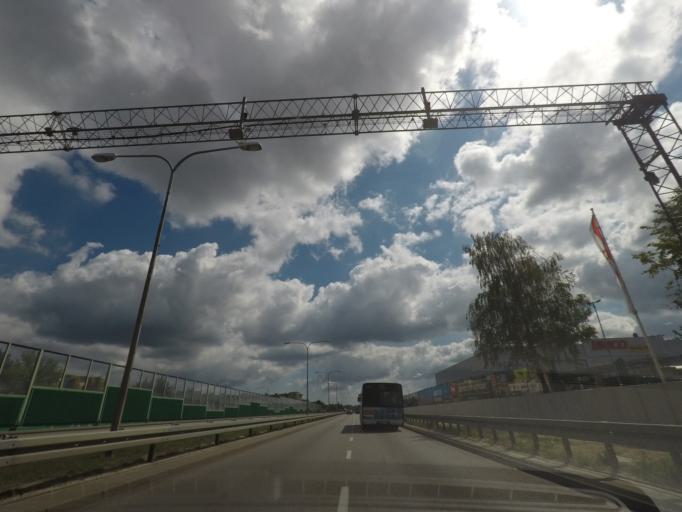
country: PL
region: Pomeranian Voivodeship
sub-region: Powiat wejherowski
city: Wejherowo
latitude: 54.6072
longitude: 18.2268
